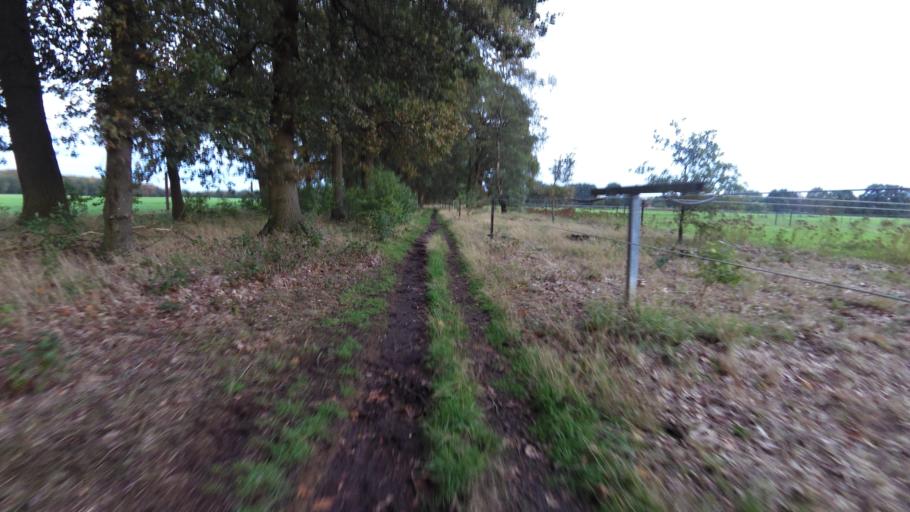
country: NL
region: Gelderland
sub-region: Gemeente Renkum
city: Wolfheze
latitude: 52.0138
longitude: 5.7906
